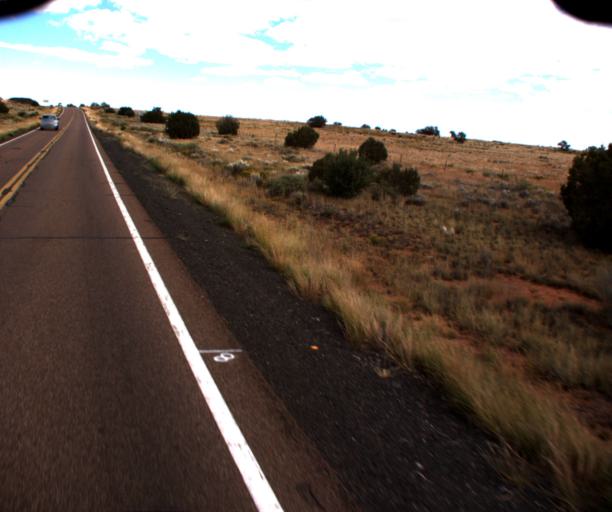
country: US
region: Arizona
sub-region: Navajo County
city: Snowflake
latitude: 34.6459
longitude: -110.3498
